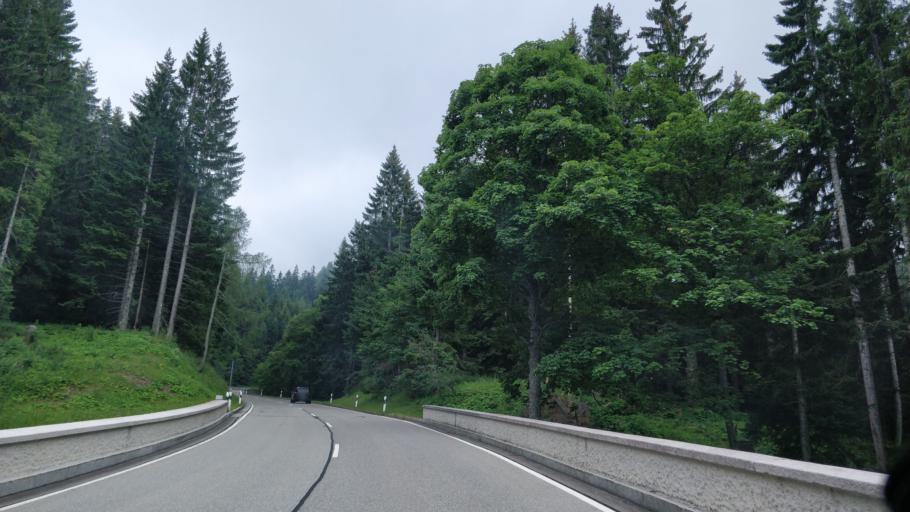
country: AT
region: Salzburg
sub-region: Politischer Bezirk Hallein
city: Hallein
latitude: 47.6378
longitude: 13.0916
